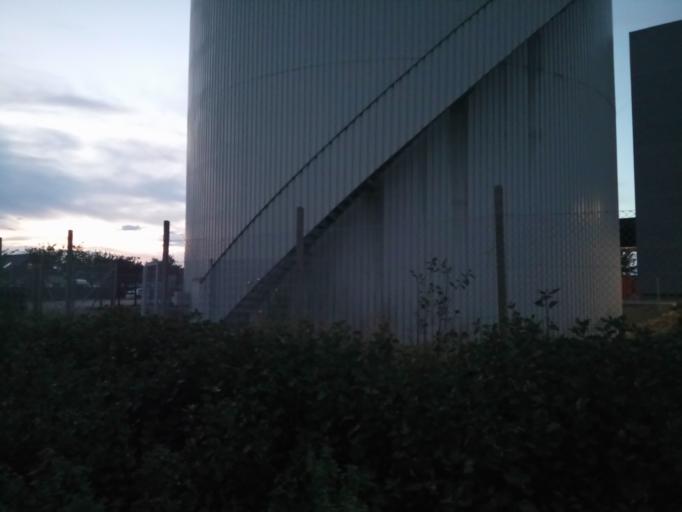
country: DK
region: Central Jutland
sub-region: Ringkobing-Skjern Kommune
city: Skjern
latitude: 55.9495
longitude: 8.5090
